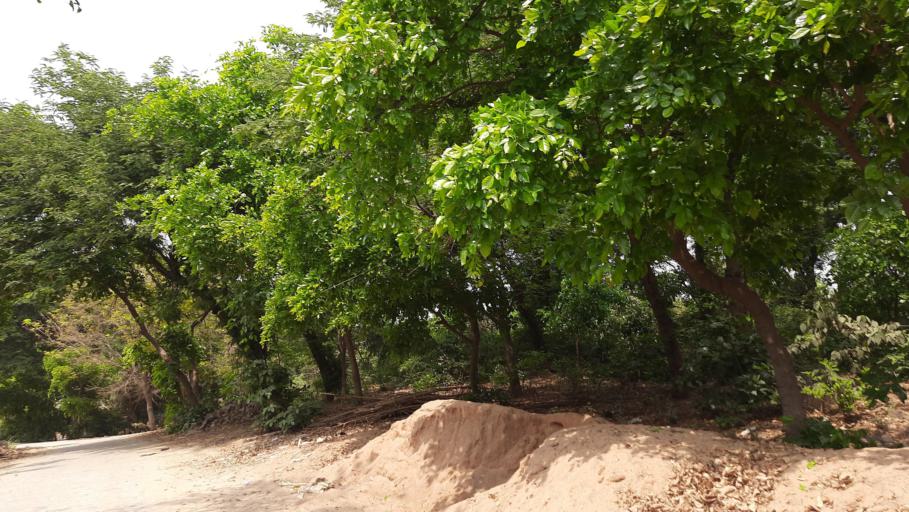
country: IN
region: Uttar Pradesh
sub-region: Faizabad
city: Ayodhya
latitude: 26.7836
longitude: 82.1860
